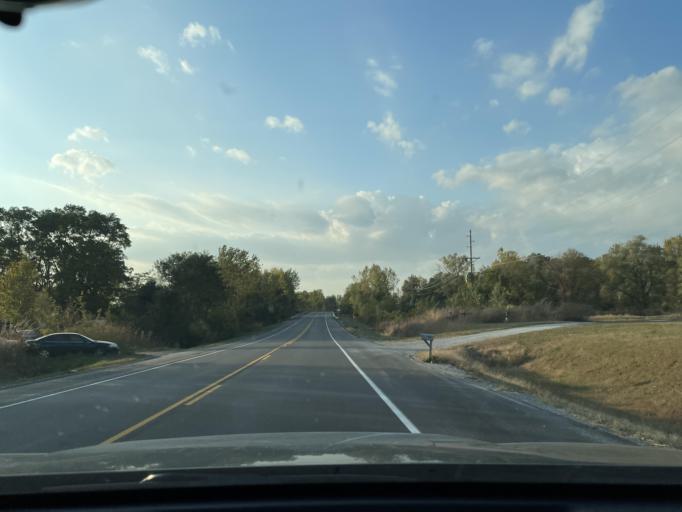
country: US
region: Missouri
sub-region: Andrew County
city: Country Club Village
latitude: 39.8577
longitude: -94.8769
